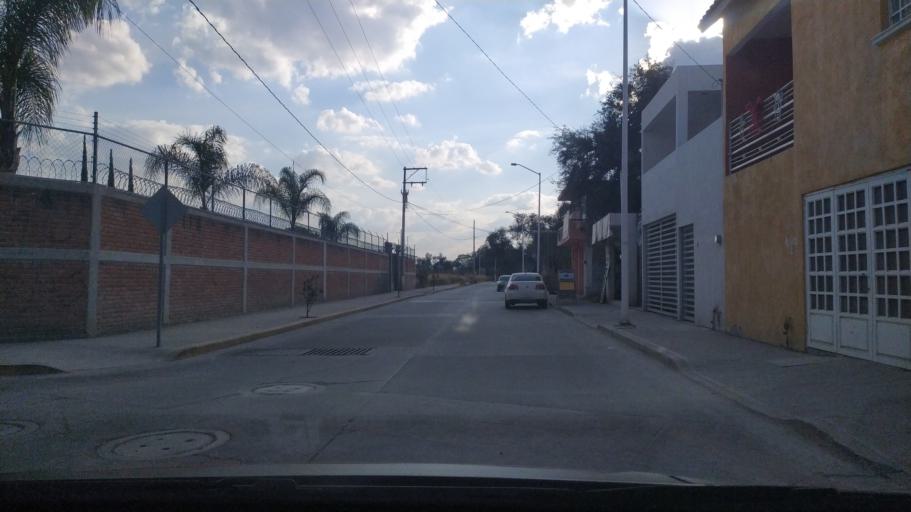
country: MX
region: Guanajuato
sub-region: Purisima del Rincon
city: Monte Grande
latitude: 21.0092
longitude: -101.8689
